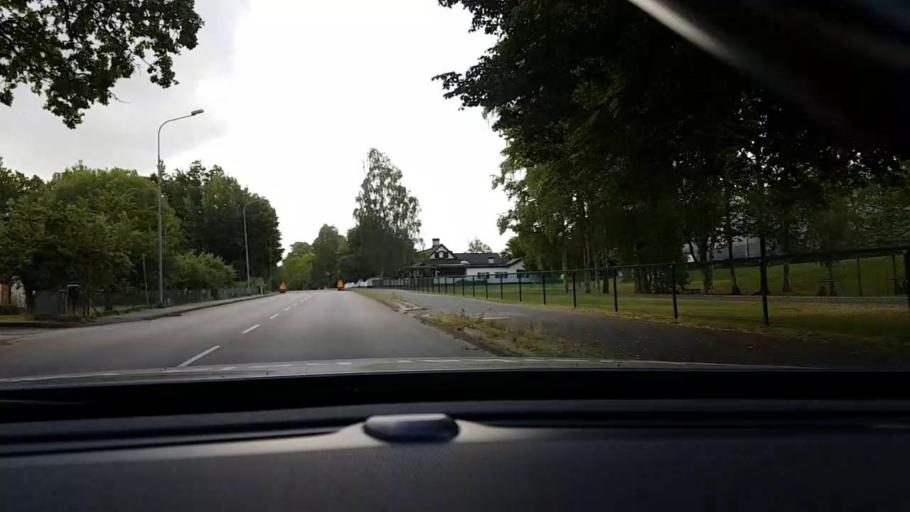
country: SE
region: Skane
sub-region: Hassleholms Kommun
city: Hassleholm
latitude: 56.1664
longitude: 13.7485
